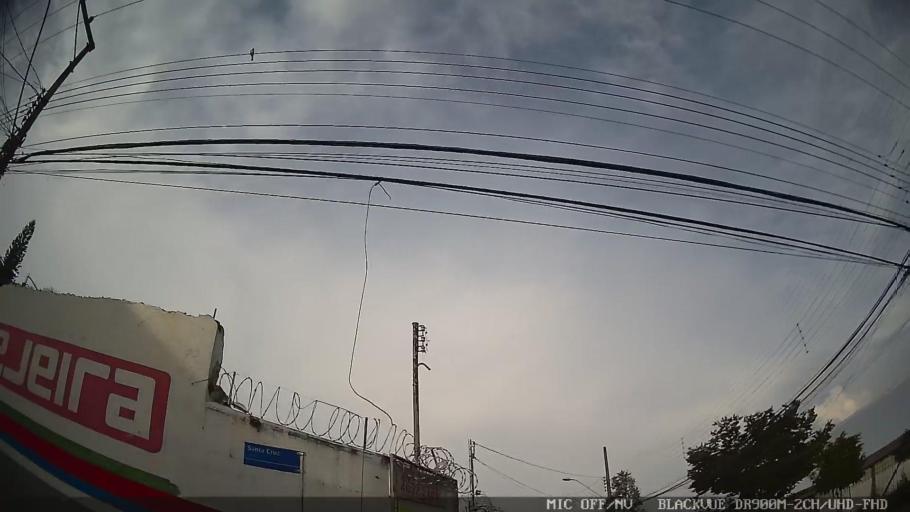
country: BR
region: Sao Paulo
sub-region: Braganca Paulista
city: Braganca Paulista
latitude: -22.9425
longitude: -46.5521
